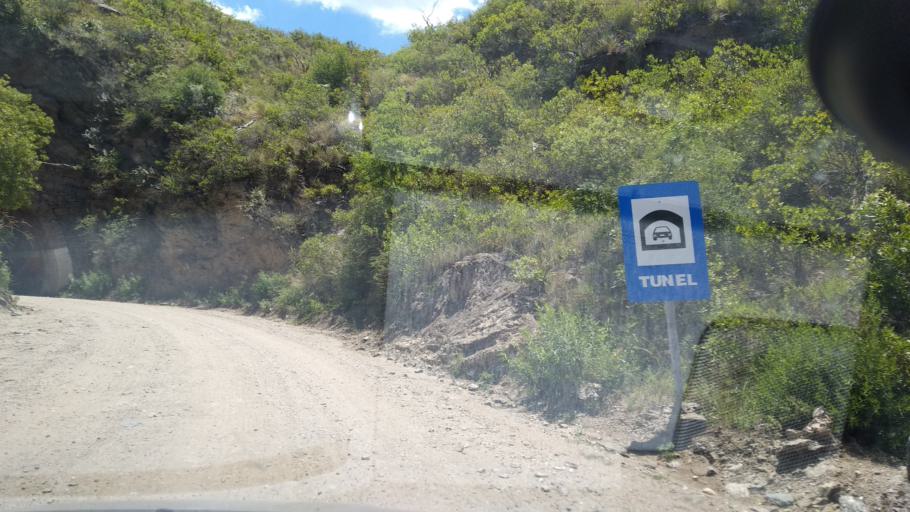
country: AR
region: Cordoba
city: Salsacate
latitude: -31.3781
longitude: -65.4006
